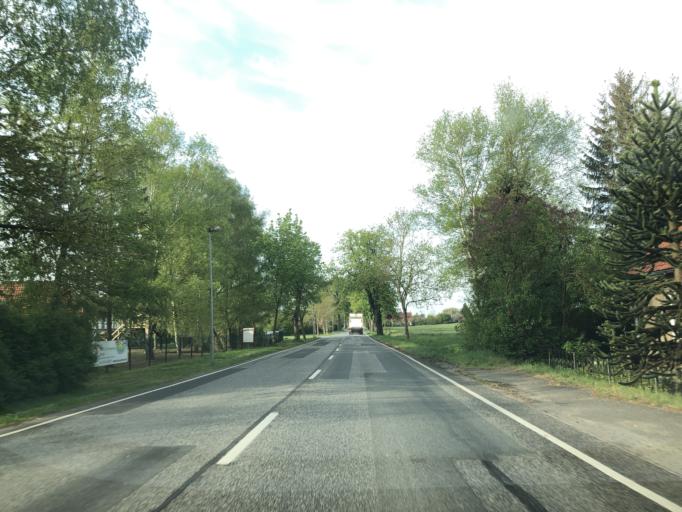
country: DE
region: Mecklenburg-Vorpommern
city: Guestrow
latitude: 53.8571
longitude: 12.2305
